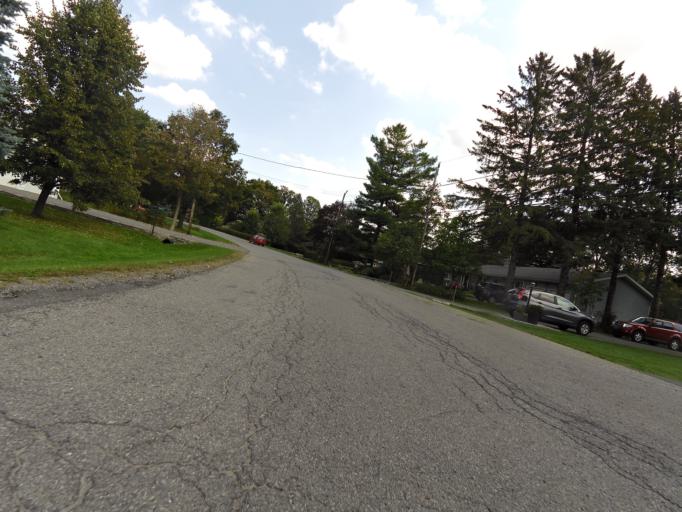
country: CA
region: Ontario
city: Bells Corners
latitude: 45.2287
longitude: -75.6876
